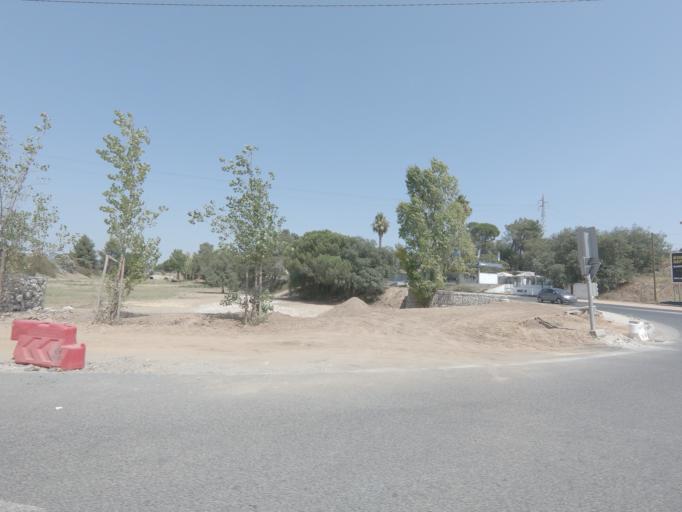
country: PT
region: Setubal
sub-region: Setubal
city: Setubal
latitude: 38.5474
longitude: -8.8848
